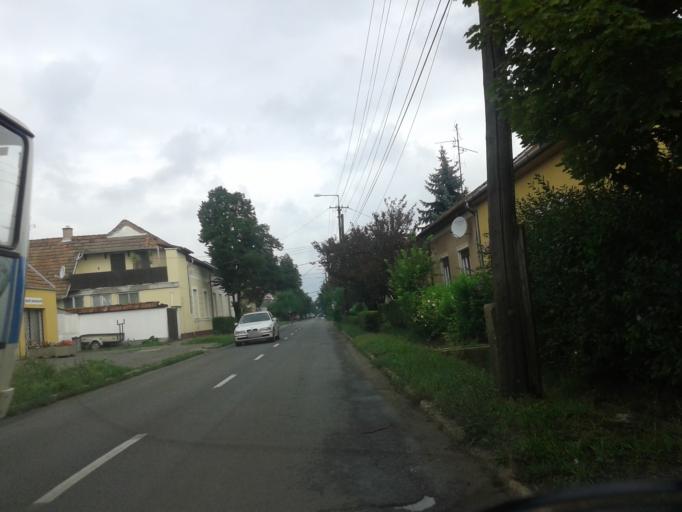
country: HU
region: Csongrad
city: Szeged
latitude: 46.2660
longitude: 20.1785
